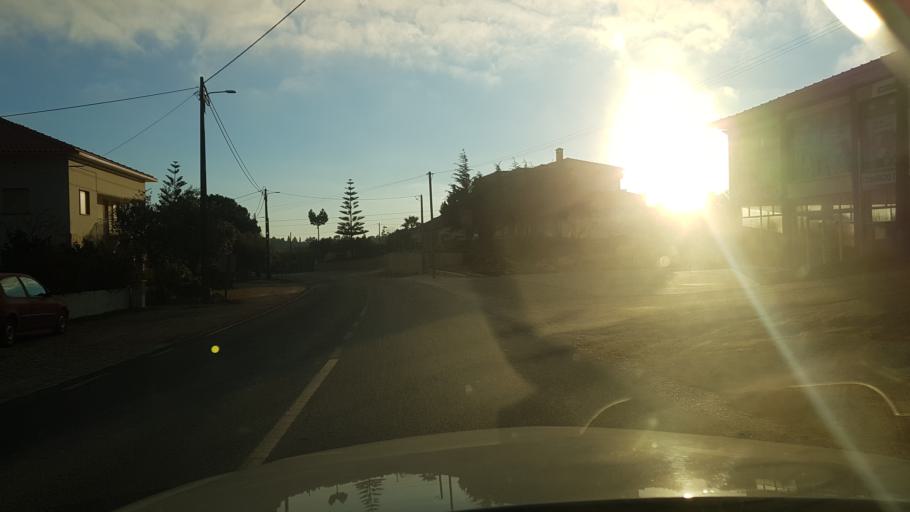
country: PT
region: Santarem
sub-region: Ourem
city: Ourem
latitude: 39.5720
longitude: -8.6005
